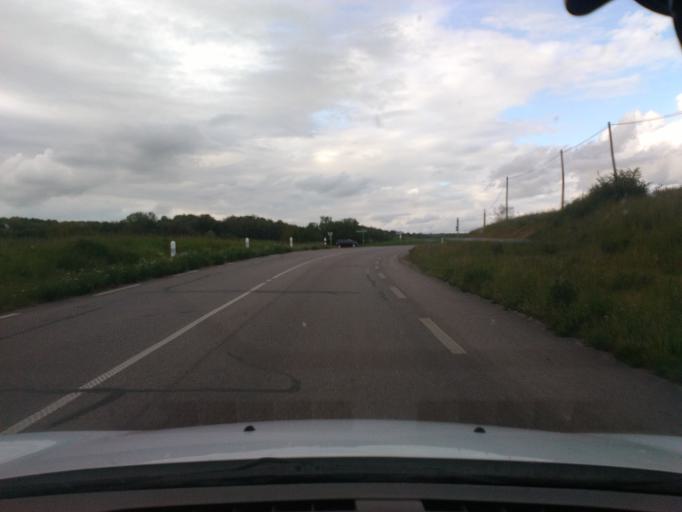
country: FR
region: Lorraine
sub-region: Departement des Vosges
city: Mirecourt
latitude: 48.3080
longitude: 6.0886
